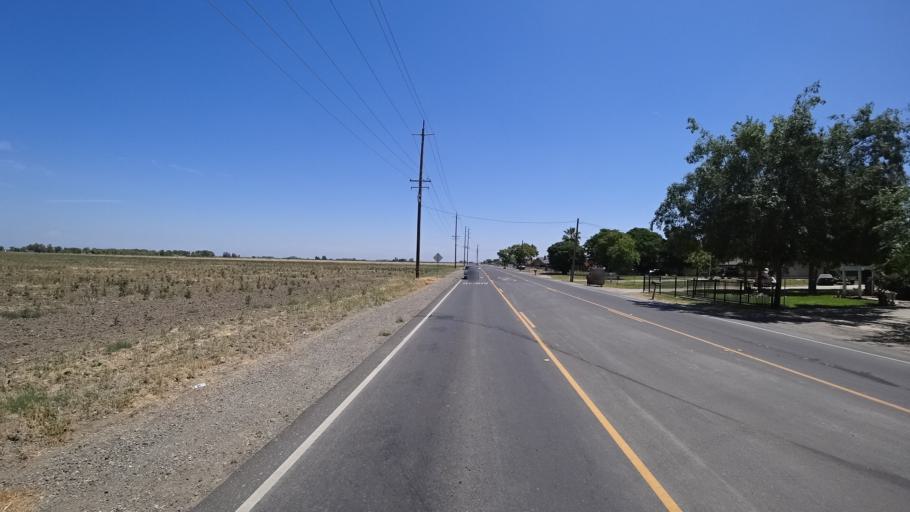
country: US
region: California
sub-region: Kings County
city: Lemoore
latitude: 36.2401
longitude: -119.7615
